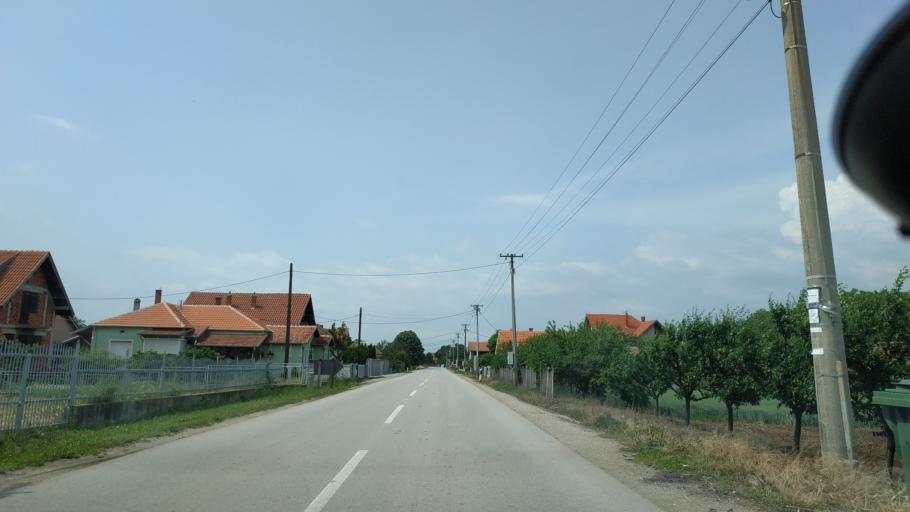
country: RS
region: Central Serbia
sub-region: Nisavski Okrug
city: Aleksinac
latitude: 43.4790
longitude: 21.7191
